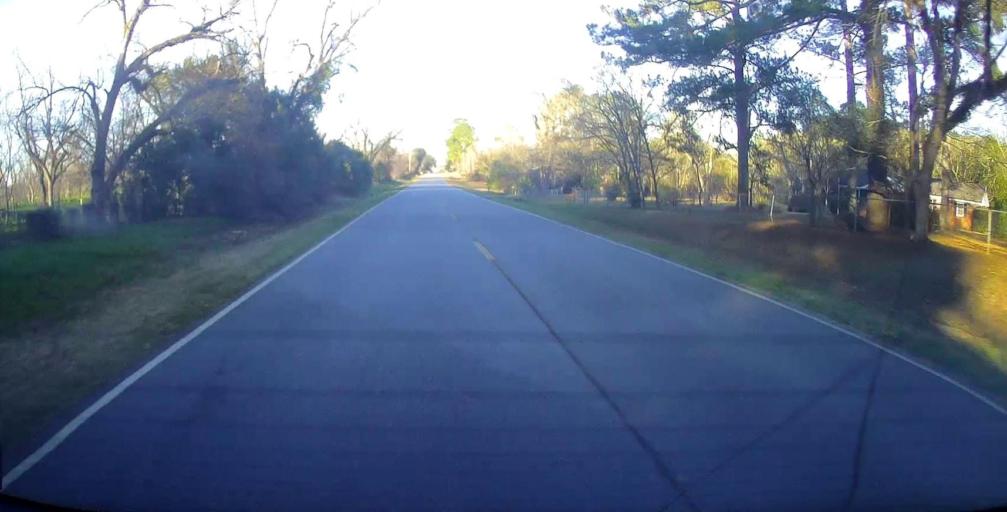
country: US
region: Georgia
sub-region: Dougherty County
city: Albany
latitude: 31.5133
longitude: -84.2354
